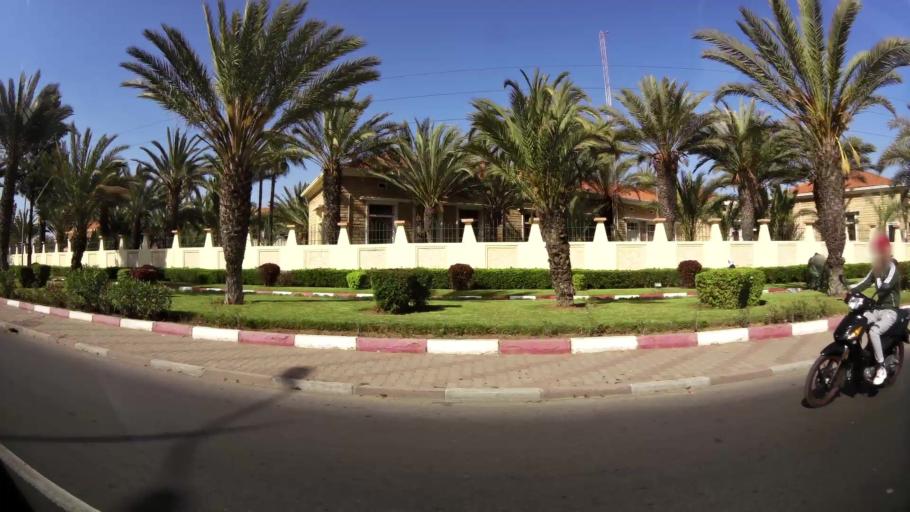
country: MA
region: Souss-Massa-Draa
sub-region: Inezgane-Ait Mellou
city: Inezgane
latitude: 30.3751
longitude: -9.5563
